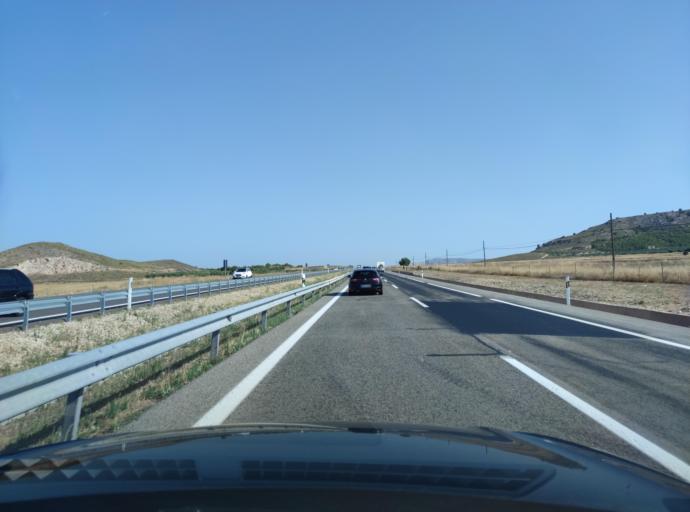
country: ES
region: Valencia
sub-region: Provincia de Alicante
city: Sax
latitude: 38.5769
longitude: -0.8414
